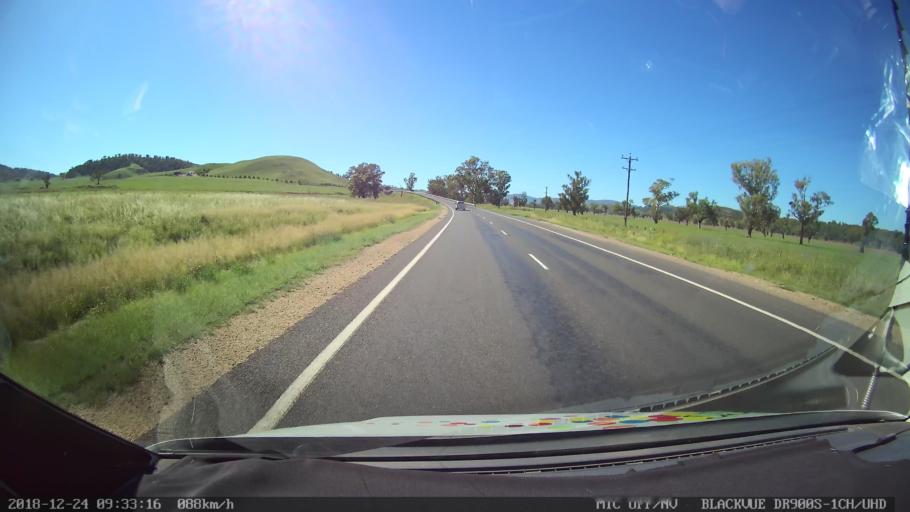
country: AU
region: New South Wales
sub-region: Liverpool Plains
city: Quirindi
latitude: -31.6016
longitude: 150.7063
